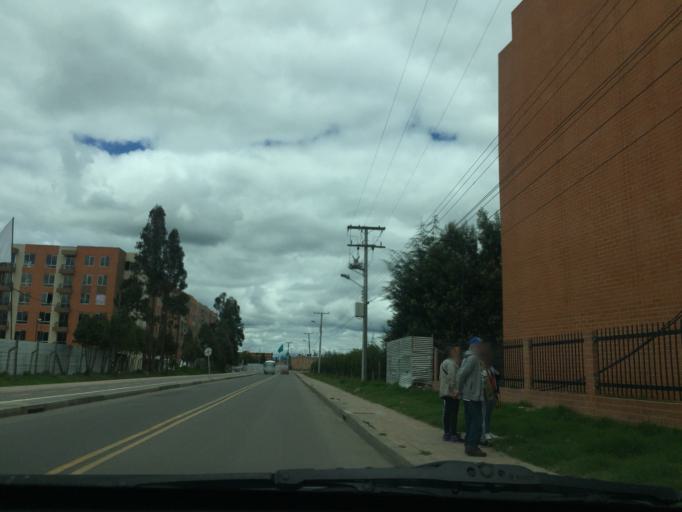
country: CO
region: Cundinamarca
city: Tocancipa
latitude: 4.9611
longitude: -73.9371
